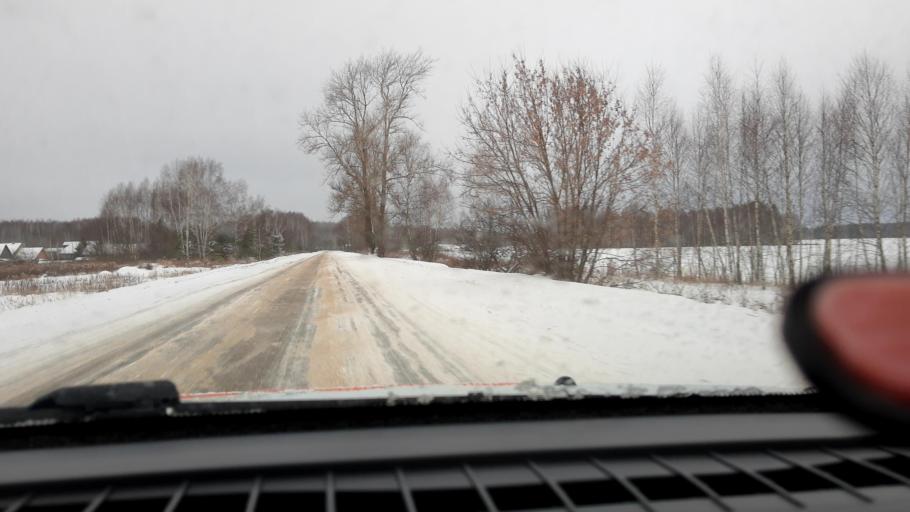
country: RU
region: Nizjnij Novgorod
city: Pamyat' Parizhskoy Kommuny
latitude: 56.2492
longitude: 44.4857
